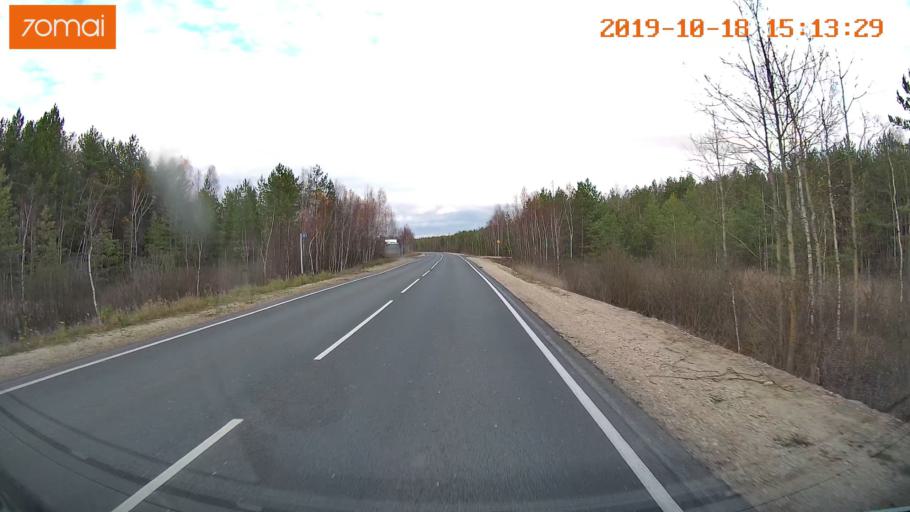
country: RU
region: Vladimir
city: Gus'-Khrustal'nyy
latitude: 55.5875
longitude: 40.7171
